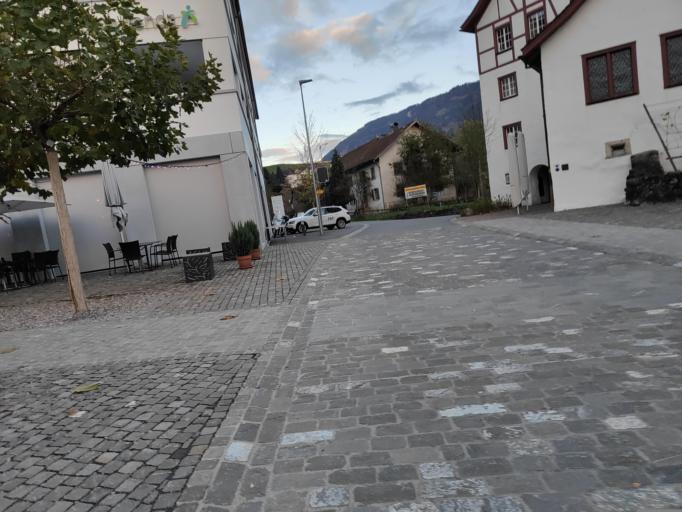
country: LI
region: Eschen
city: Eschen
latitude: 47.2123
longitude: 9.5243
